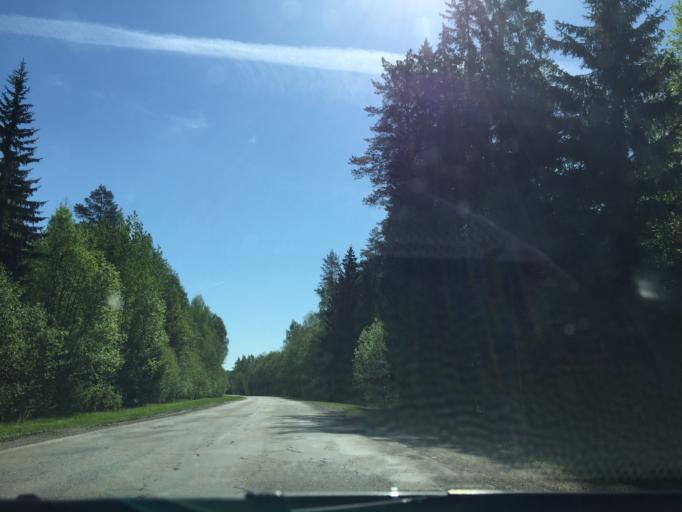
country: LV
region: Incukalns
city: Incukalns
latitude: 57.0250
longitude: 24.7519
